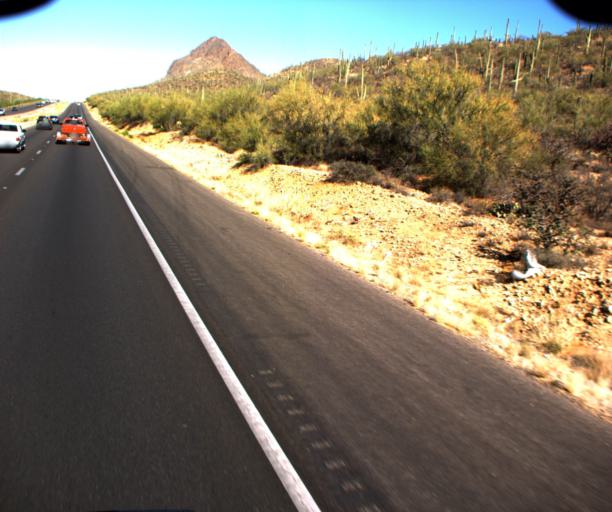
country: US
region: Arizona
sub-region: Pima County
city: Drexel Heights
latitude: 32.1769
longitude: -111.0309
